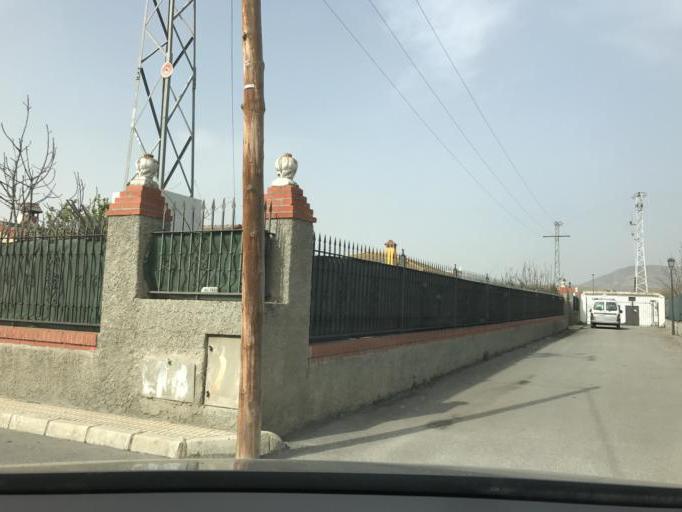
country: ES
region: Andalusia
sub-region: Provincia de Granada
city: Atarfe
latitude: 37.1958
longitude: -3.6763
